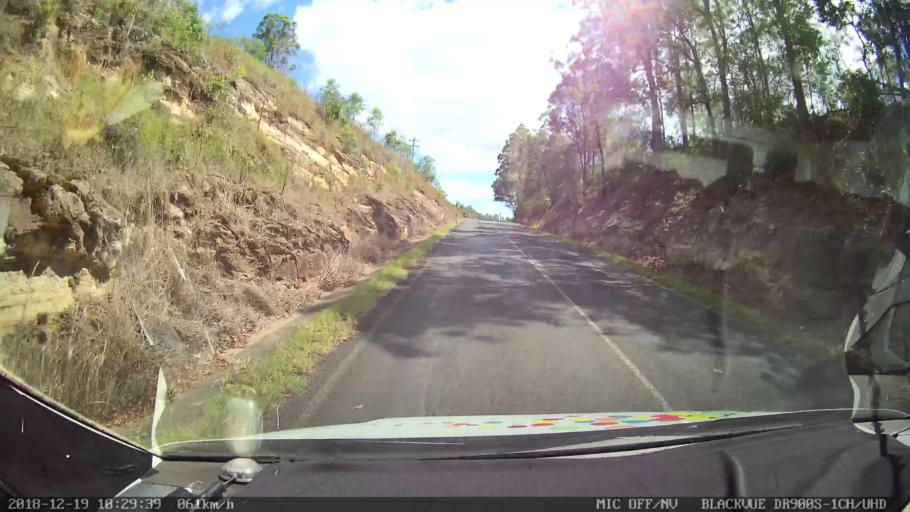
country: AU
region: New South Wales
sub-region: Lismore Municipality
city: Larnook
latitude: -28.5943
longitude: 153.1013
